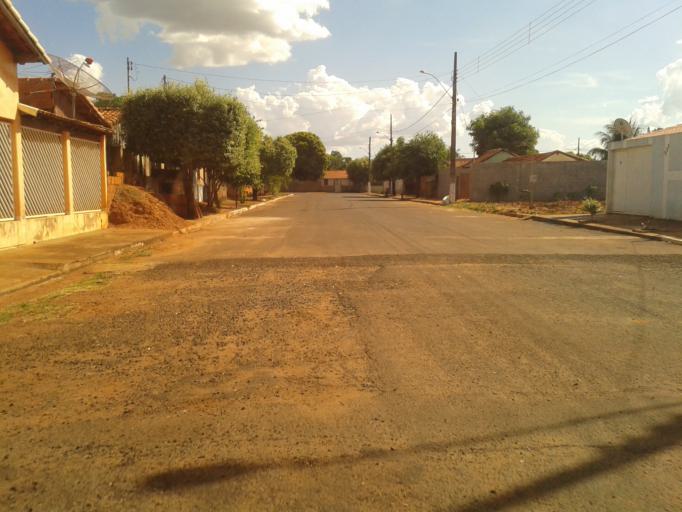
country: BR
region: Minas Gerais
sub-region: Santa Vitoria
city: Santa Vitoria
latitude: -18.6960
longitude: -49.9423
